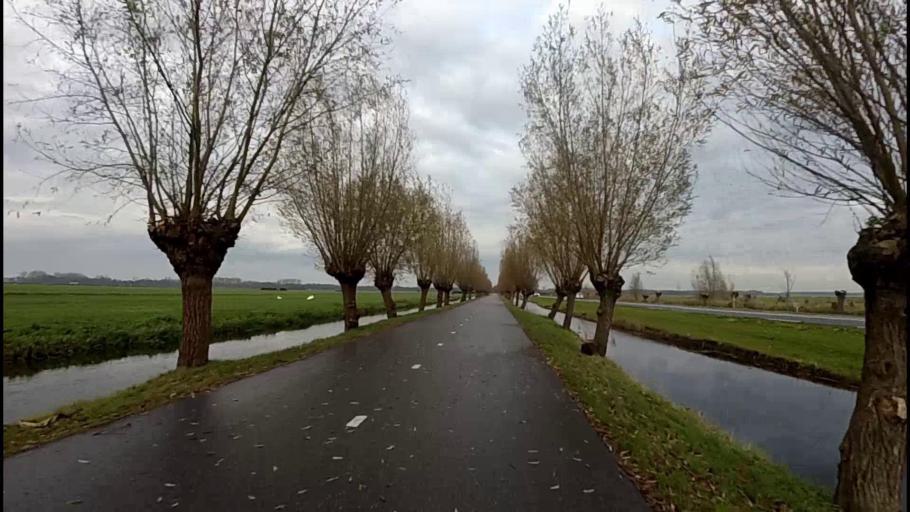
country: NL
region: South Holland
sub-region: Molenwaard
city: Nieuw-Lekkerland
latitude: 51.9106
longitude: 4.6849
